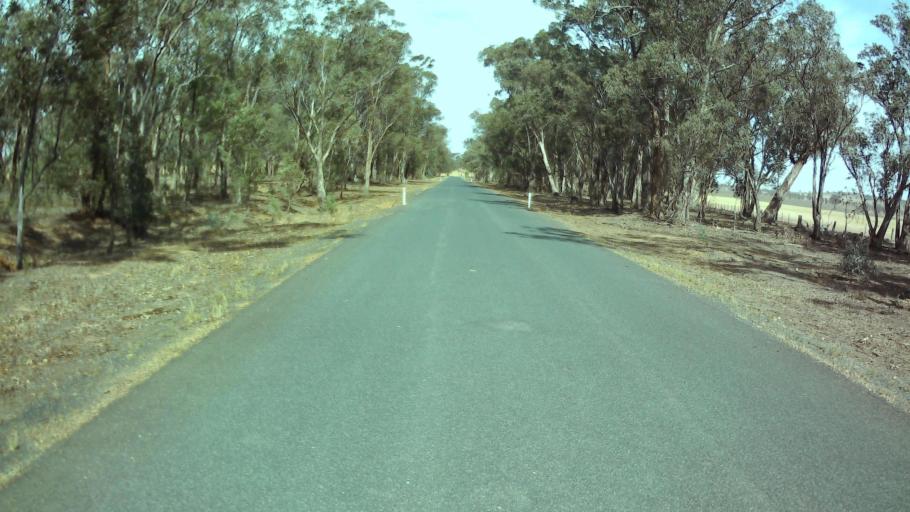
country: AU
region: New South Wales
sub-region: Weddin
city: Grenfell
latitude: -33.8086
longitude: 148.0726
